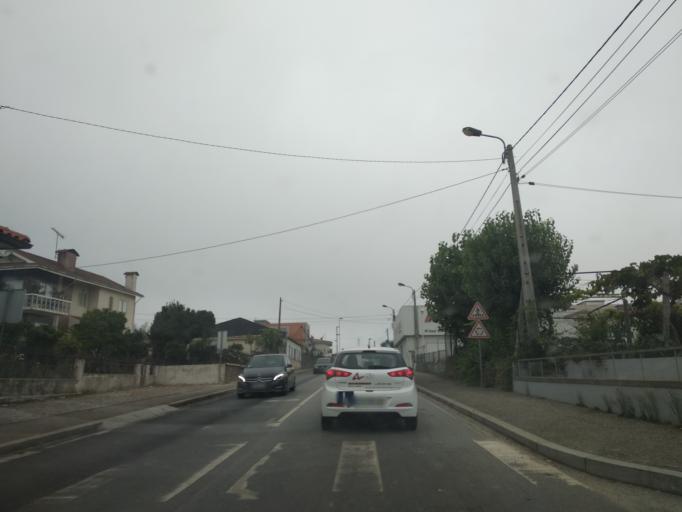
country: PT
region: Braga
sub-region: Vila Verde
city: Vila Verde
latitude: 41.6418
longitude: -8.4353
